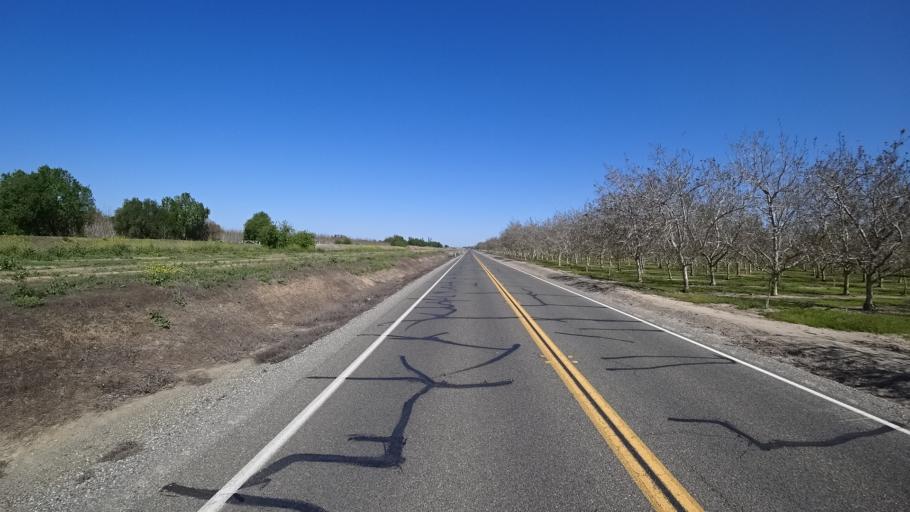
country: US
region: California
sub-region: Glenn County
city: Hamilton City
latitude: 39.7162
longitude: -122.0067
